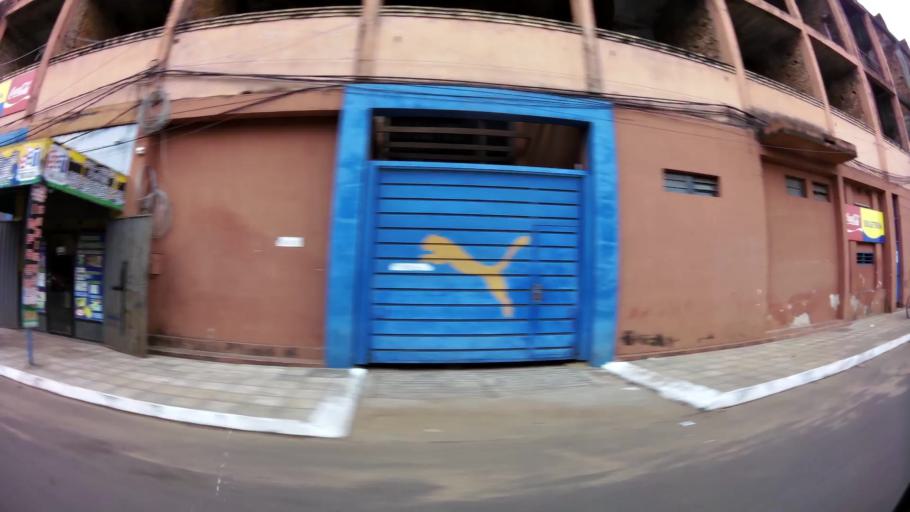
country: PY
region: Central
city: San Lorenzo
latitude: -25.2722
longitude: -57.4938
